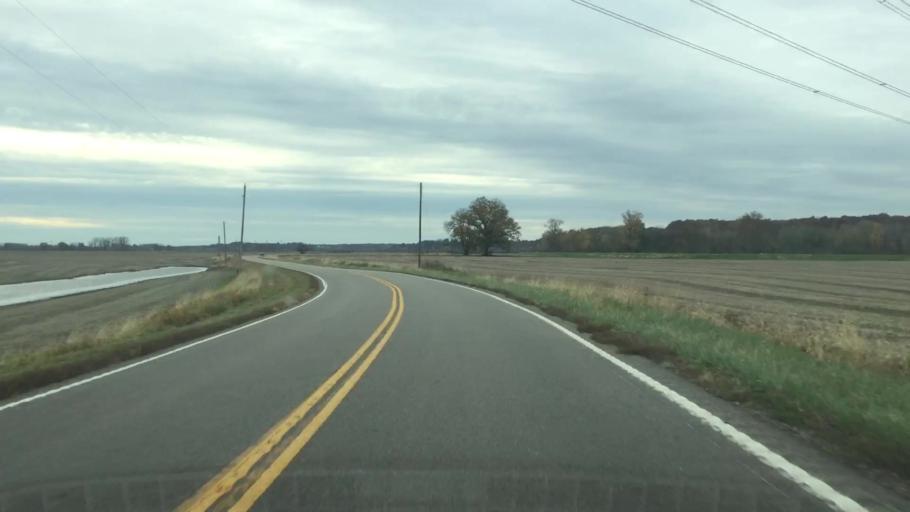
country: US
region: Missouri
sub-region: Callaway County
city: Fulton
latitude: 38.7053
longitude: -91.7691
